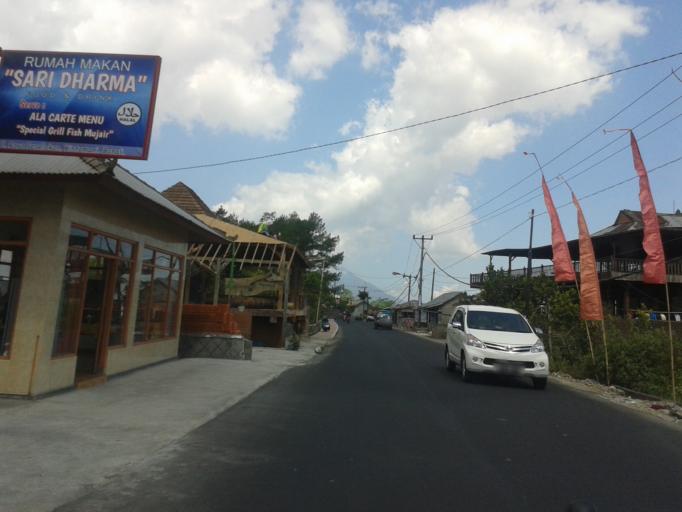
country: ID
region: Bali
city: Banjar Kedisan
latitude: -8.2776
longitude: 115.3518
